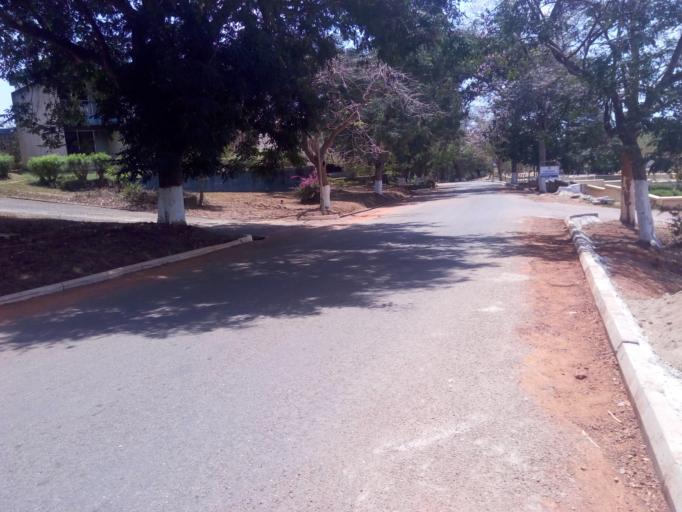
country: GH
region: Central
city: Cape Coast
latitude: 5.1054
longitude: -1.2820
